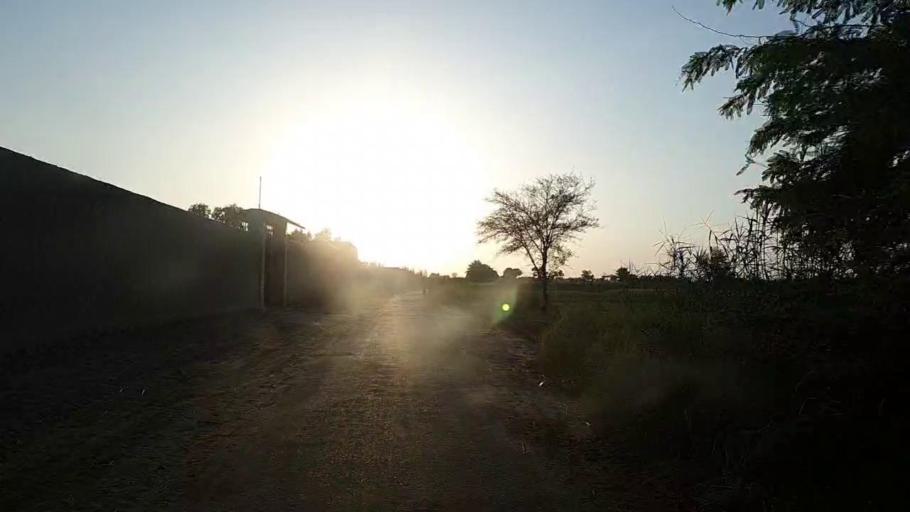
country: PK
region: Sindh
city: Hingorja
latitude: 27.0582
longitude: 68.4010
